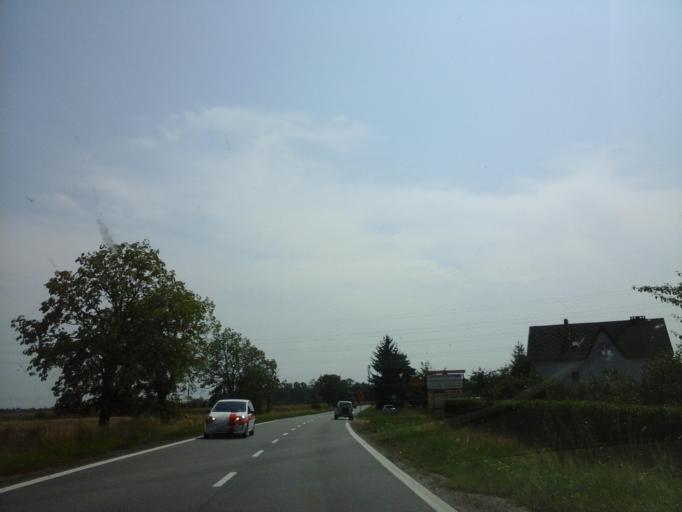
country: PL
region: Lower Silesian Voivodeship
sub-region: Powiat wroclawski
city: Zerniki Wroclawskie
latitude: 51.0376
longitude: 17.0644
